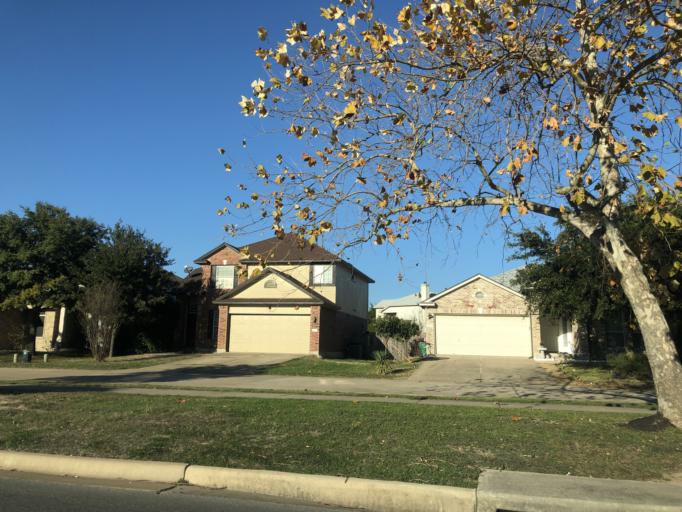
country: US
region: Texas
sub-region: Travis County
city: Windemere
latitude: 30.4727
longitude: -97.6541
